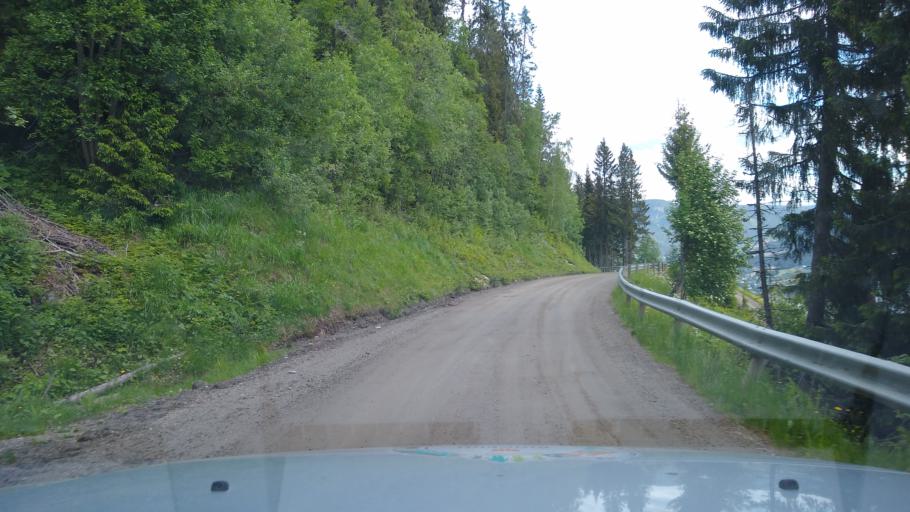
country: NO
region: Oppland
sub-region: Ringebu
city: Ringebu
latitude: 61.4999
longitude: 10.1407
